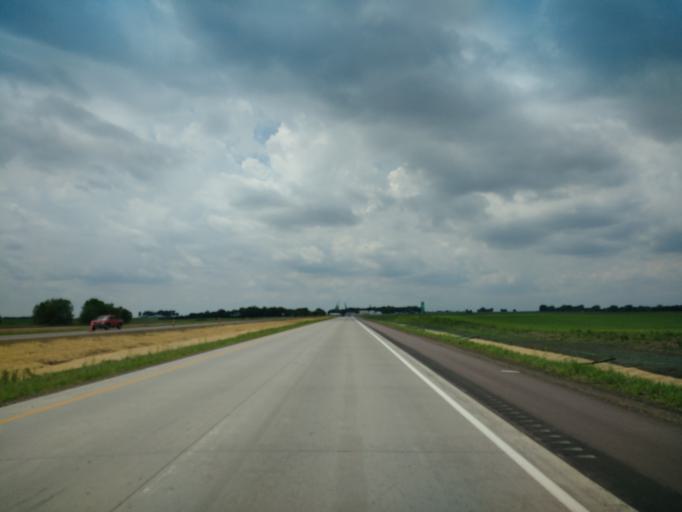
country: US
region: Minnesota
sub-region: Cottonwood County
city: Mountain Lake
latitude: 43.9128
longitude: -95.0217
